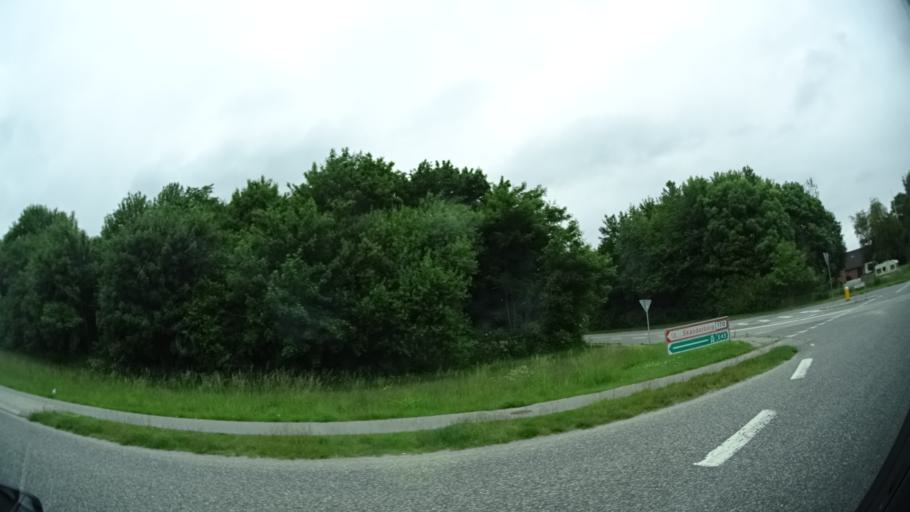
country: DK
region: Central Jutland
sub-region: Arhus Kommune
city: Kolt
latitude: 56.1034
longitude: 10.0786
